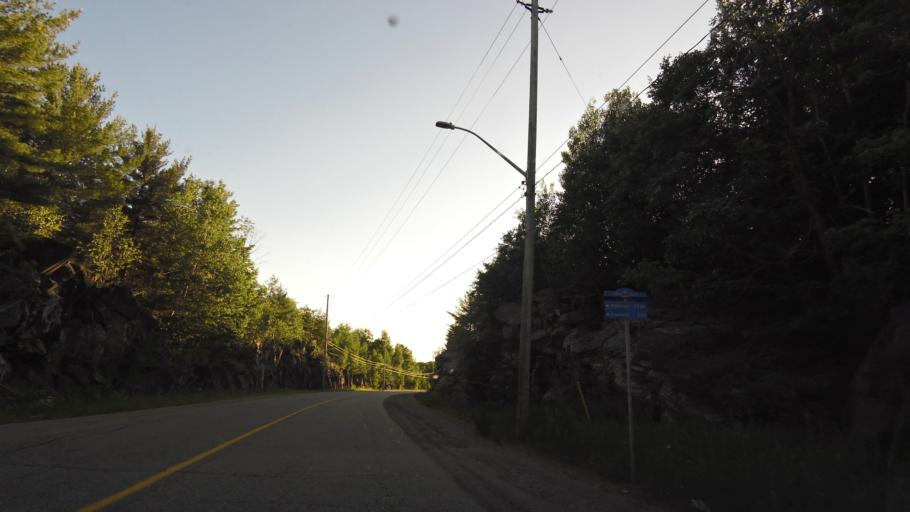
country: CA
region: Ontario
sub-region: Parry Sound District
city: Parry Sound
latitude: 45.3599
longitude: -80.0343
